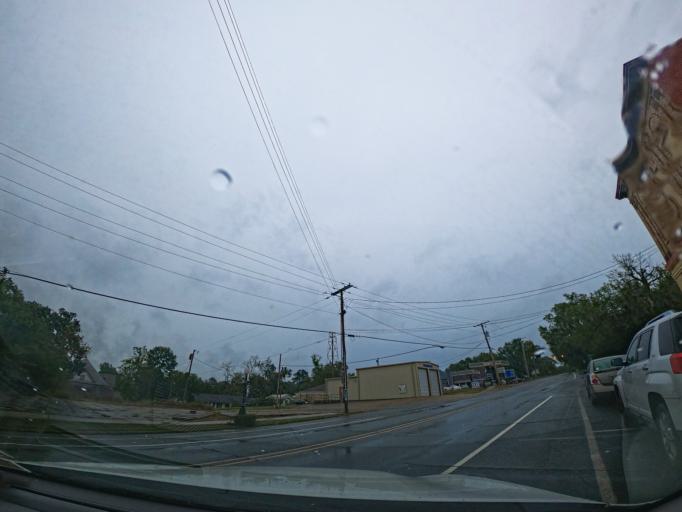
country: US
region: Louisiana
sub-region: Bienville Parish
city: Arcadia
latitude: 32.5448
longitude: -93.0531
